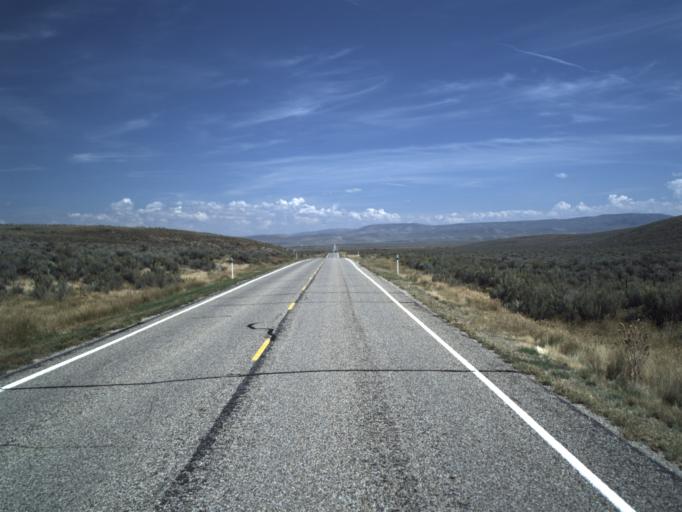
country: US
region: Utah
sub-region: Rich County
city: Randolph
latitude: 41.7688
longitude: -111.1618
